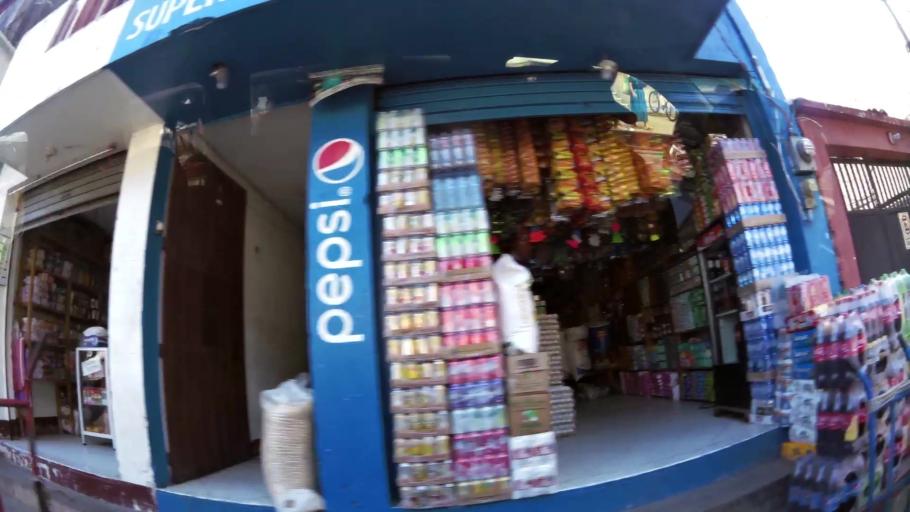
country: GT
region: Solola
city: Panajachel
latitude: 14.7465
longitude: -91.1533
